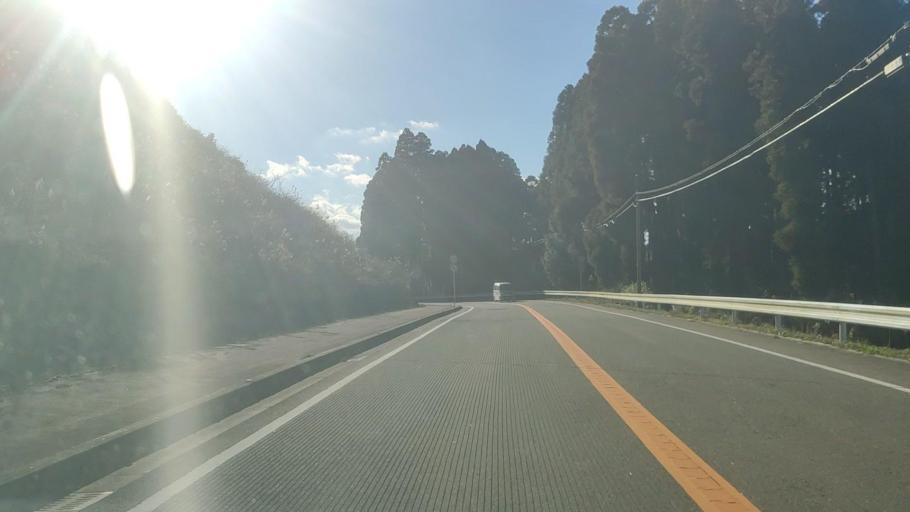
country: JP
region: Fukuoka
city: Maebaru-chuo
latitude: 33.4413
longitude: 130.2679
